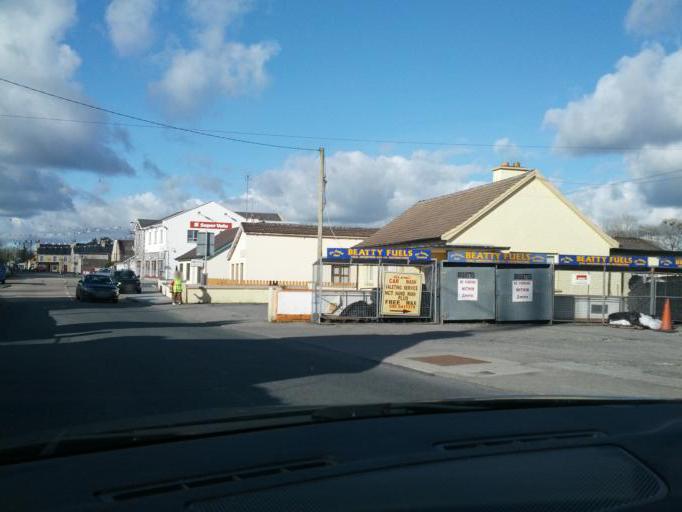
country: IE
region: Connaught
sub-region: Roscommon
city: Castlerea
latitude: 53.6047
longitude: -8.5606
